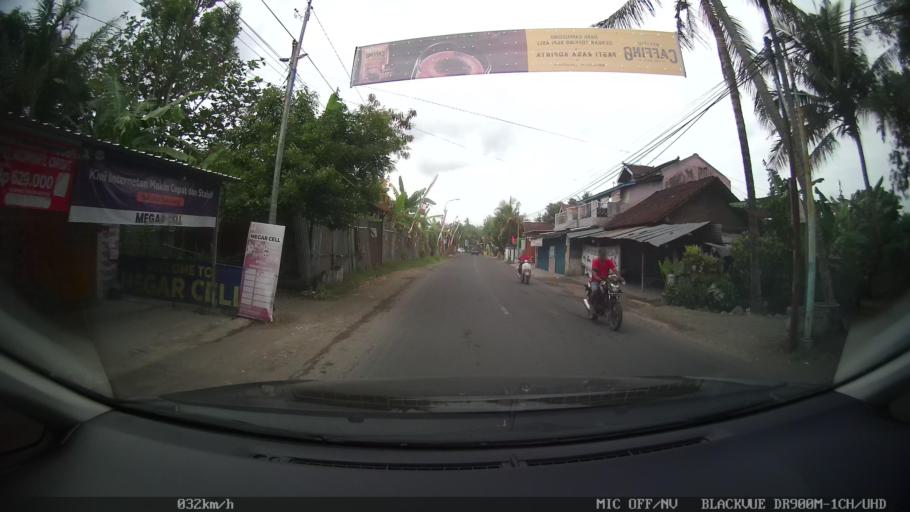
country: ID
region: Daerah Istimewa Yogyakarta
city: Sewon
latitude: -7.8687
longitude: 110.4076
